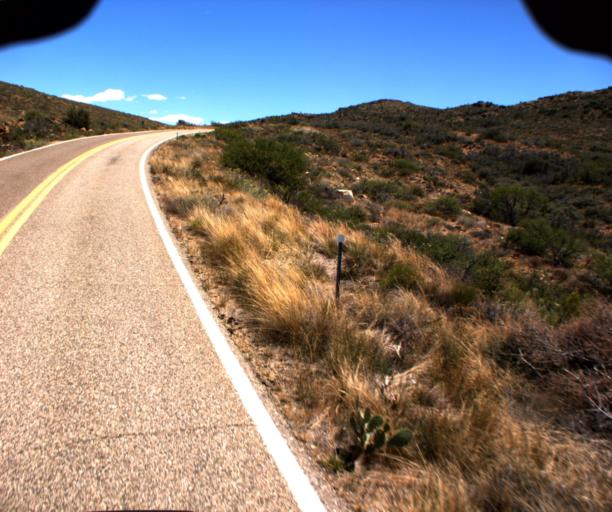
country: US
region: Arizona
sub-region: Yavapai County
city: Bagdad
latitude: 34.4456
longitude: -112.9573
